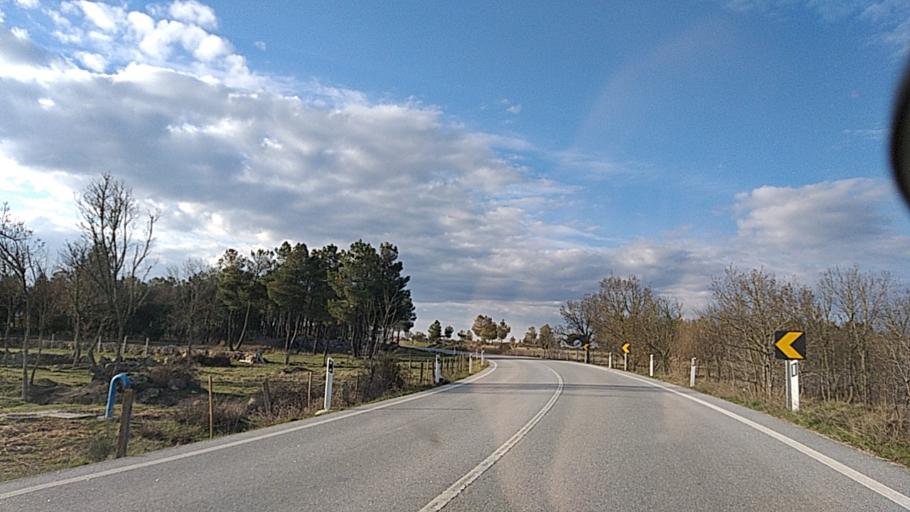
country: ES
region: Castille and Leon
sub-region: Provincia de Salamanca
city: Aldea del Obispo
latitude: 40.6696
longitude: -6.8592
